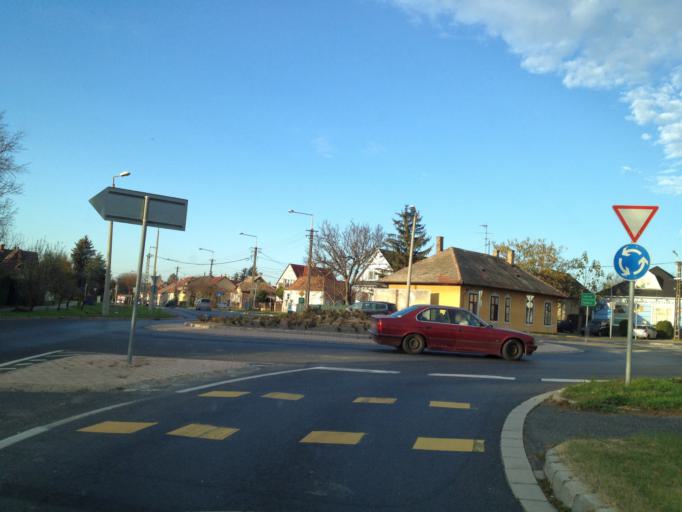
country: HU
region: Gyor-Moson-Sopron
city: Gyor
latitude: 47.6533
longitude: 17.6589
